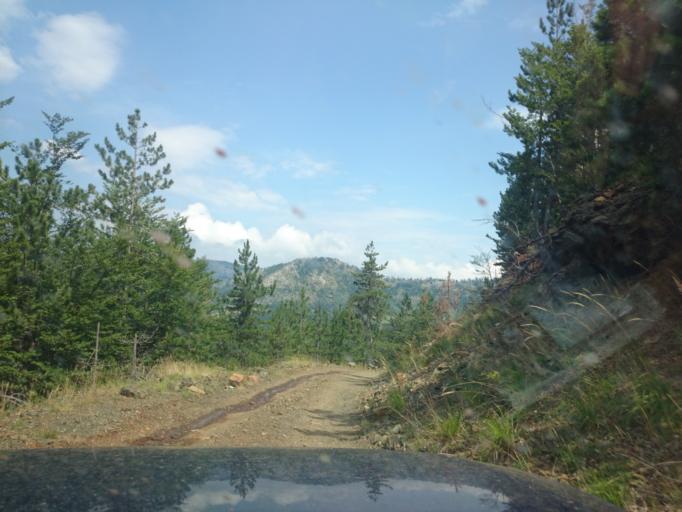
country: AL
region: Lezhe
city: Kurbnesh
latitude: 41.7951
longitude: 20.1540
